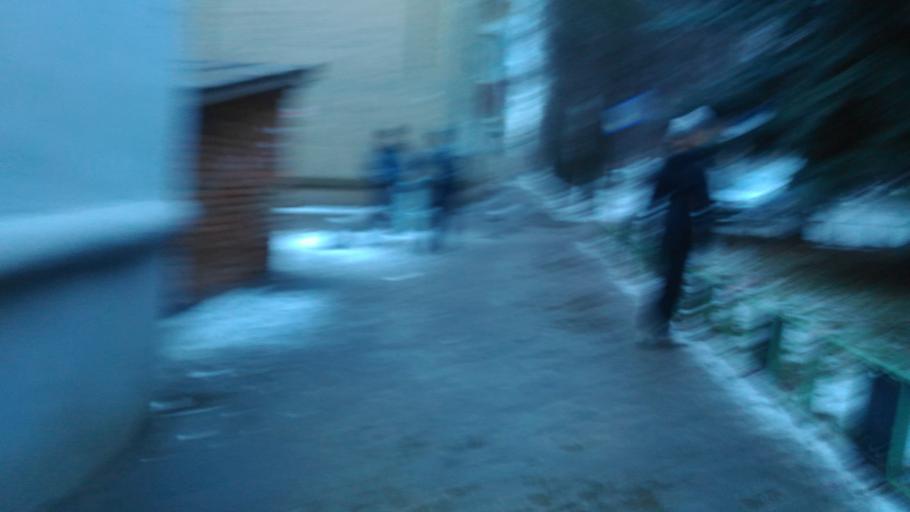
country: RU
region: Tula
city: Tula
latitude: 54.1773
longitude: 37.6029
